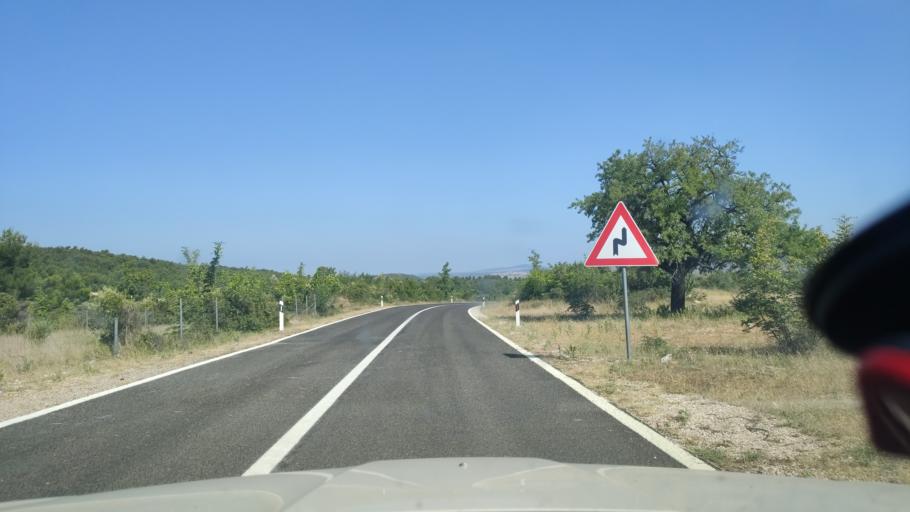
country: HR
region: Sibensko-Kniniska
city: Zaton
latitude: 43.9118
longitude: 15.8384
